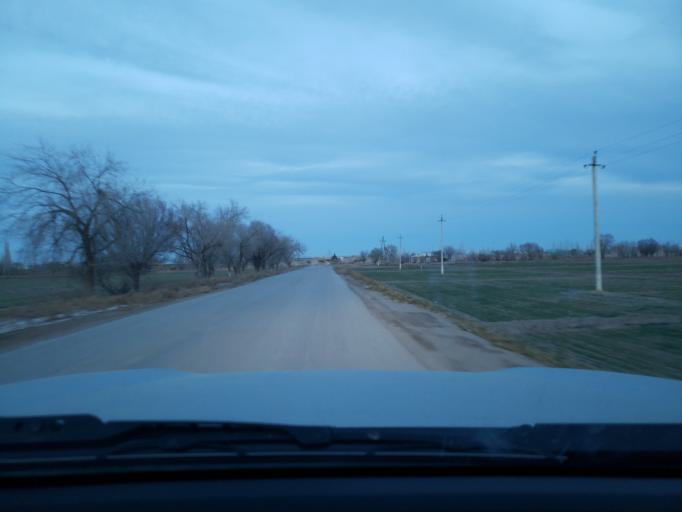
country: TM
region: Dasoguz
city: Tagta
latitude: 41.6283
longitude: 60.0655
